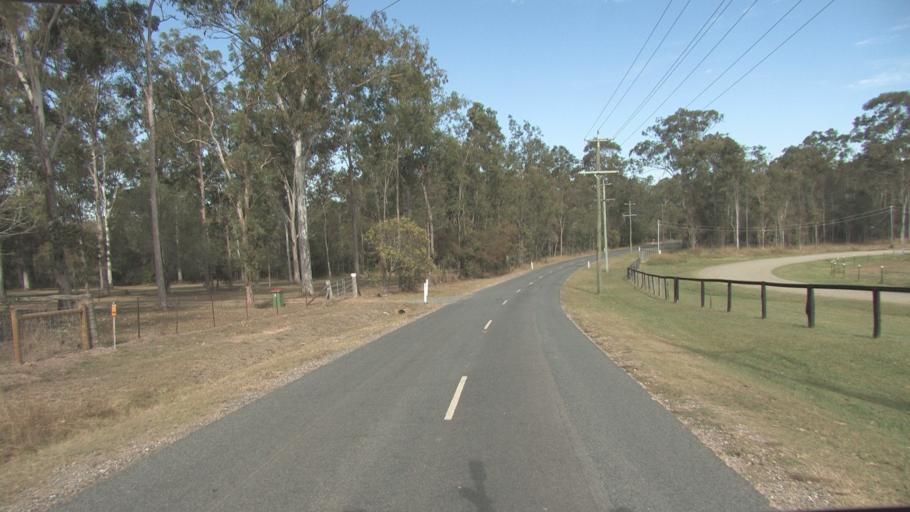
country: AU
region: Queensland
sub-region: Logan
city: North Maclean
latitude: -27.7560
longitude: 152.9745
